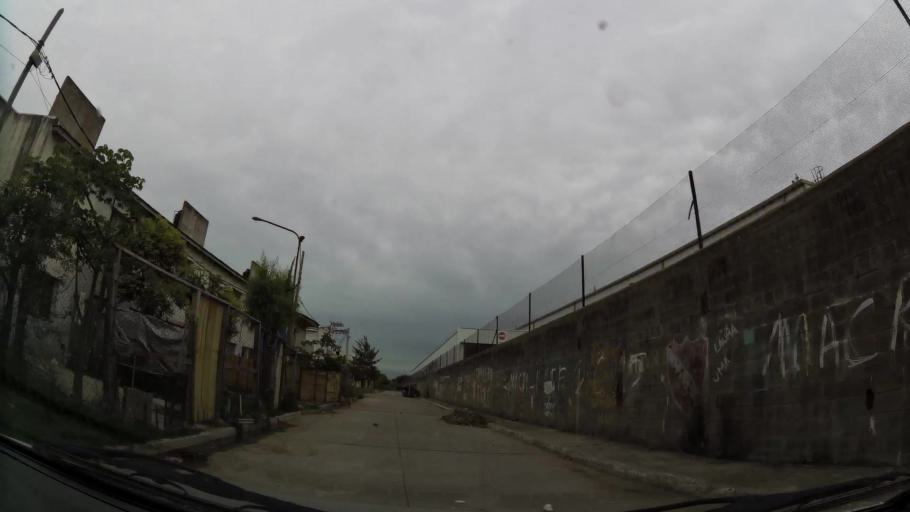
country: AR
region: Buenos Aires
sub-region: Partido de Avellaneda
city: Avellaneda
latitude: -34.6483
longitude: -58.3567
